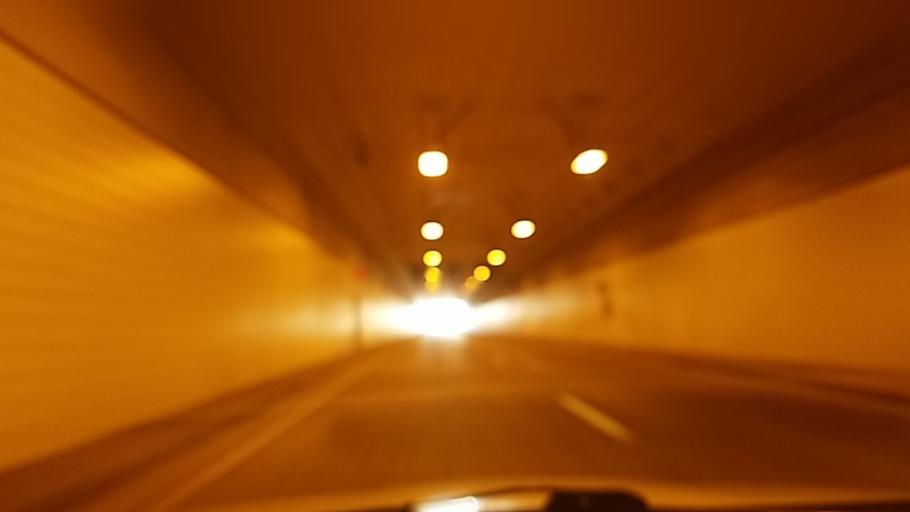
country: US
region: Minnesota
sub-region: Hennepin County
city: Richfield
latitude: 44.8768
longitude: -93.2377
